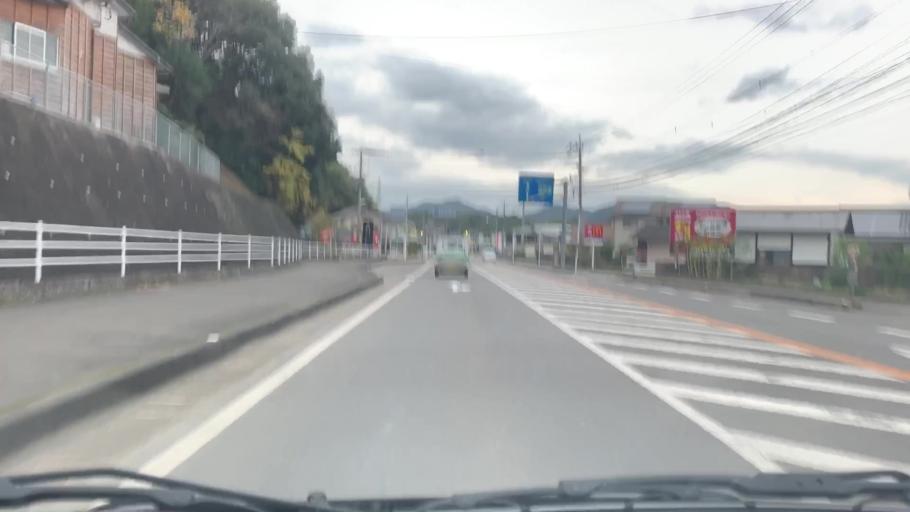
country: JP
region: Saga Prefecture
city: Takeocho-takeo
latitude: 33.1846
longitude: 130.0387
